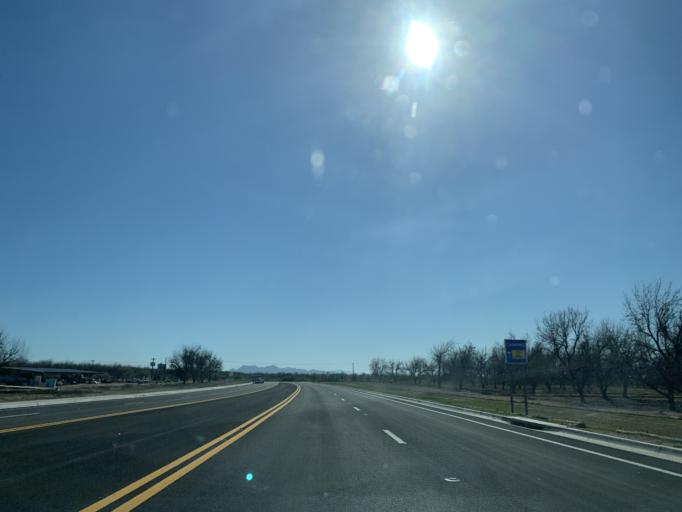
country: US
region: Arizona
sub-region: Pinal County
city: Eloy
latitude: 32.7221
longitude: -111.5175
